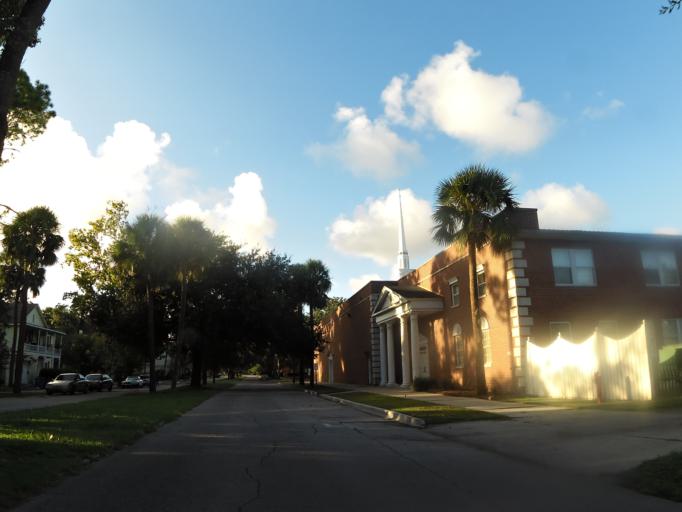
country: US
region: Georgia
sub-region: Glynn County
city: Brunswick
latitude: 31.1462
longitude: -81.4920
